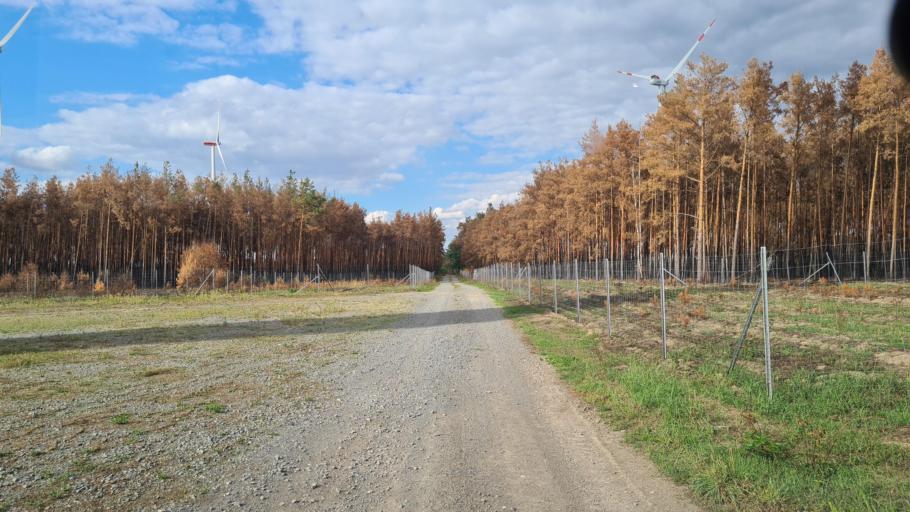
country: DE
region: Saxony
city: Arzberg
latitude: 51.5627
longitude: 13.1792
